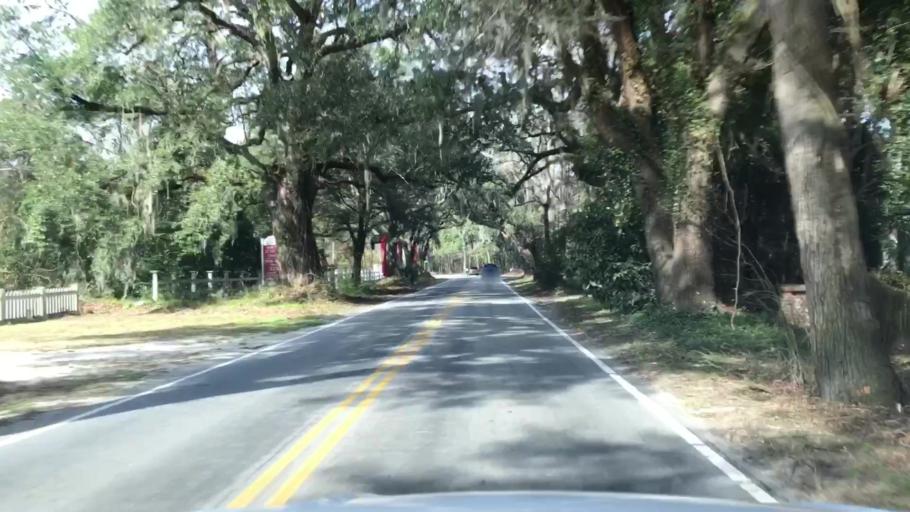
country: US
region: South Carolina
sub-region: Charleston County
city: Shell Point
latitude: 32.7513
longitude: -80.0442
